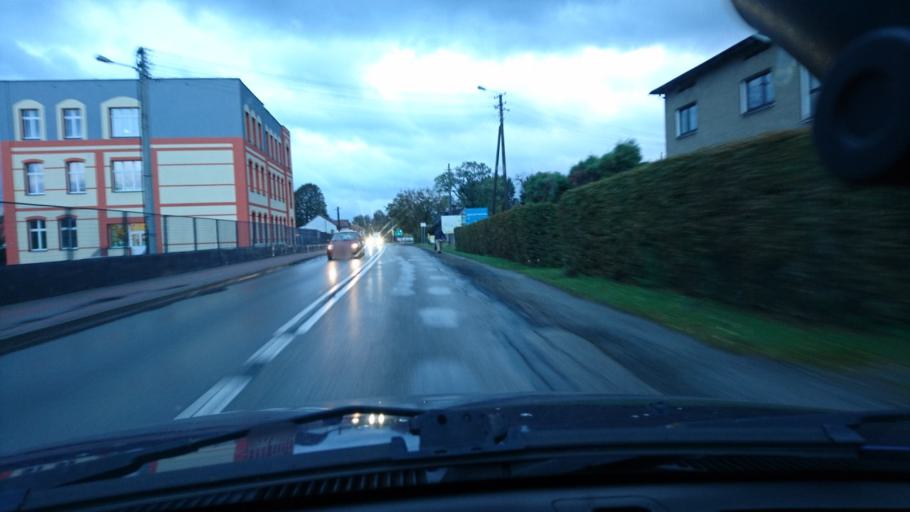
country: PL
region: Silesian Voivodeship
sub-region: Powiat bielski
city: Buczkowice
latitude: 49.7308
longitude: 19.0682
